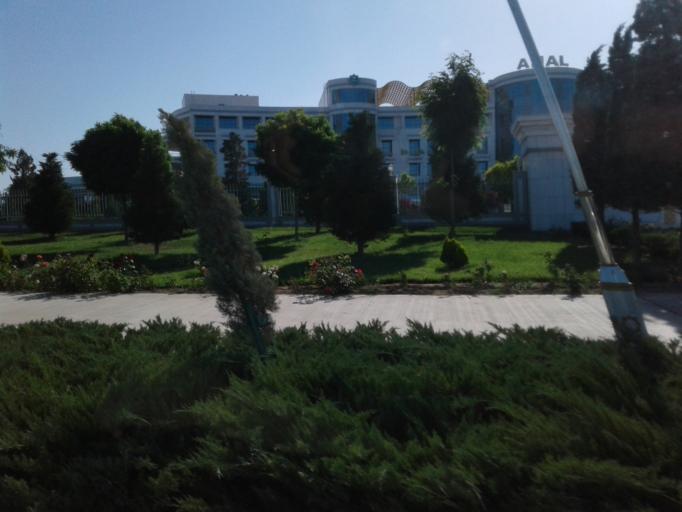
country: TM
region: Balkan
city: Turkmenbasy
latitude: 39.9842
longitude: 52.8257
